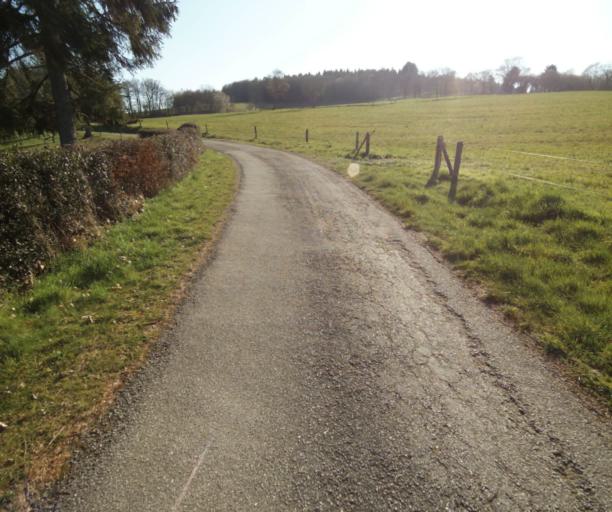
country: FR
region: Limousin
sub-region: Departement de la Correze
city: Chamboulive
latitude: 45.4851
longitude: 1.7313
